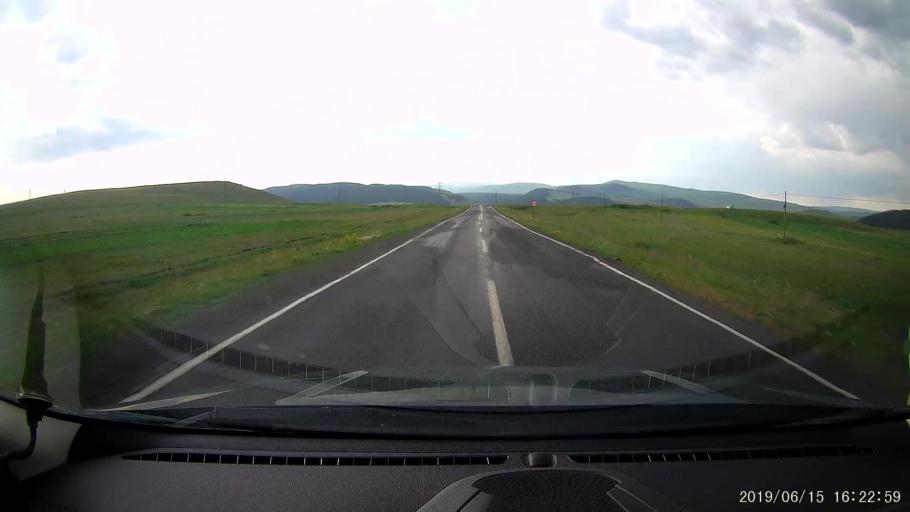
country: TR
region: Ardahan
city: Hanak
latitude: 41.1824
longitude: 42.8566
